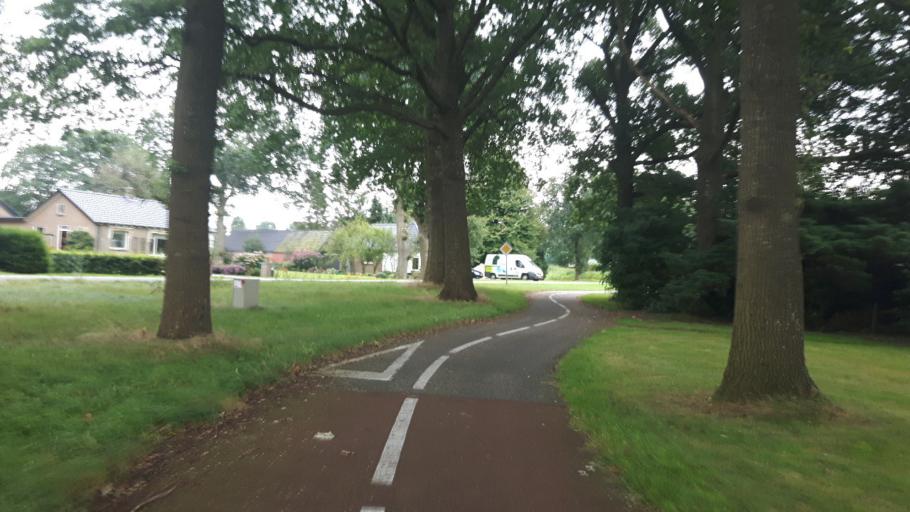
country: NL
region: Friesland
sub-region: Gemeente Weststellingwerf
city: Noordwolde
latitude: 52.9578
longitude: 6.2206
